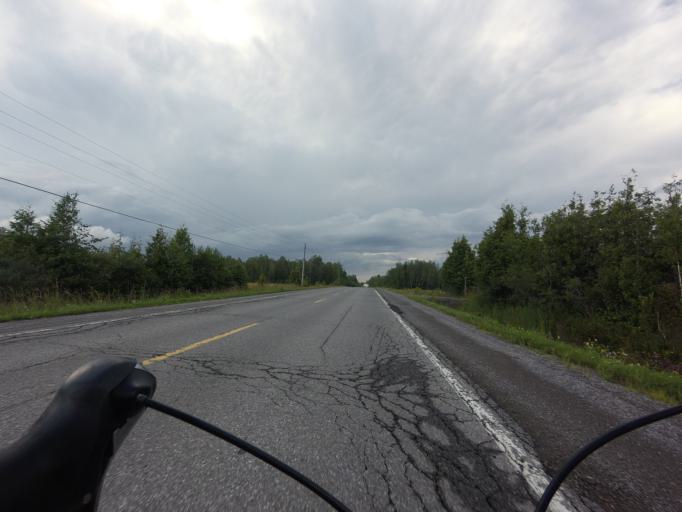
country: CA
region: Ontario
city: Carleton Place
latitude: 45.1142
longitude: -75.9300
